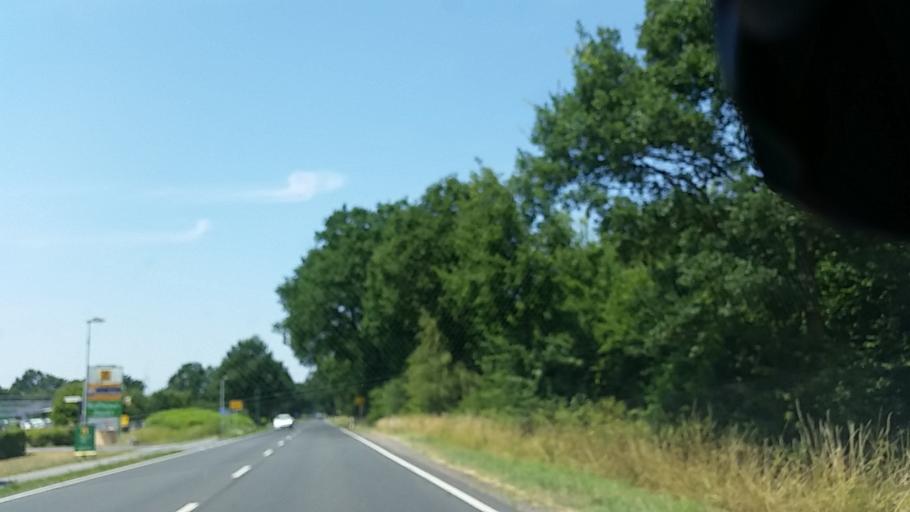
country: DE
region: Lower Saxony
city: Wietzen
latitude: 52.7126
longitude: 9.0689
